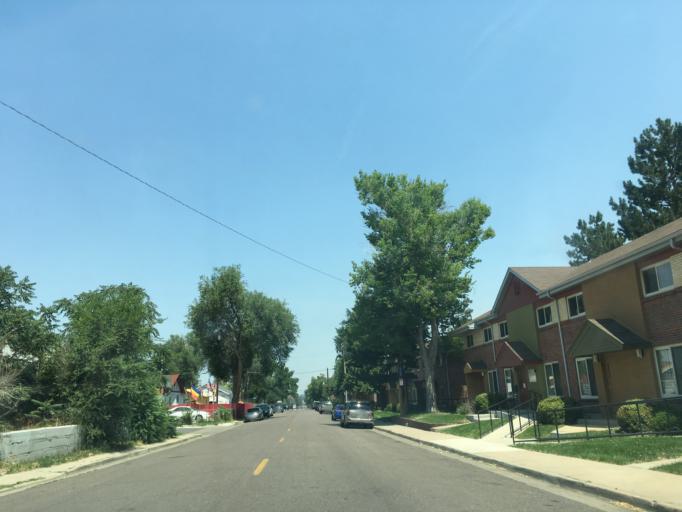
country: US
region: Colorado
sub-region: Jefferson County
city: Lakewood
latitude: 39.7009
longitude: -105.0325
